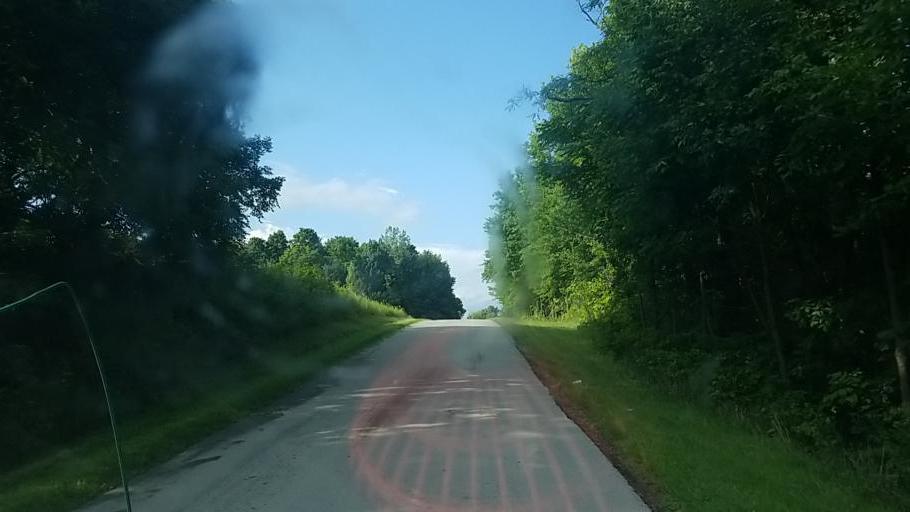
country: US
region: Ohio
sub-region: Wyandot County
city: Upper Sandusky
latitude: 40.7930
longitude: -83.3523
